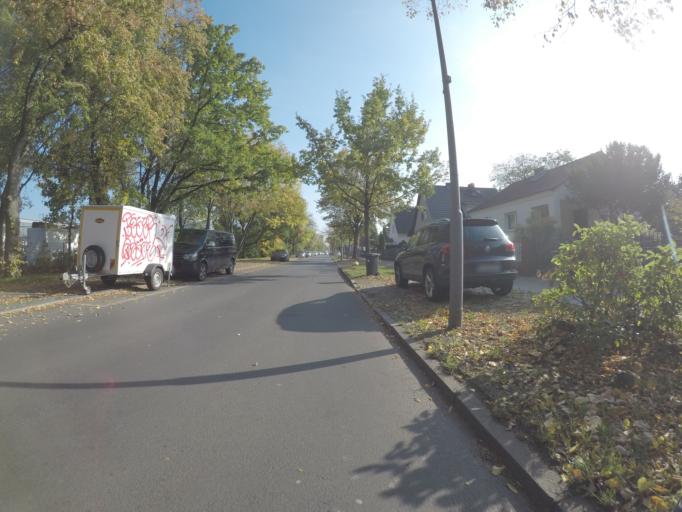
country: DE
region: Berlin
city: Rudow
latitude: 52.4331
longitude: 13.4921
